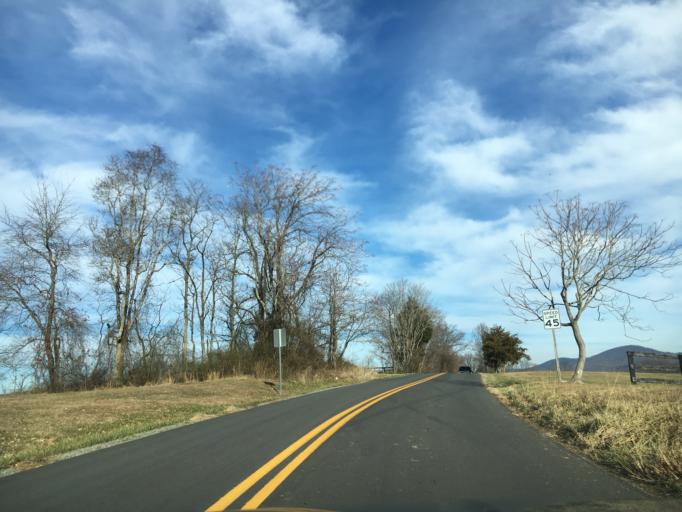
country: US
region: Virginia
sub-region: Warren County
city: Apple Mountain Lake
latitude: 38.8383
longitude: -77.9997
